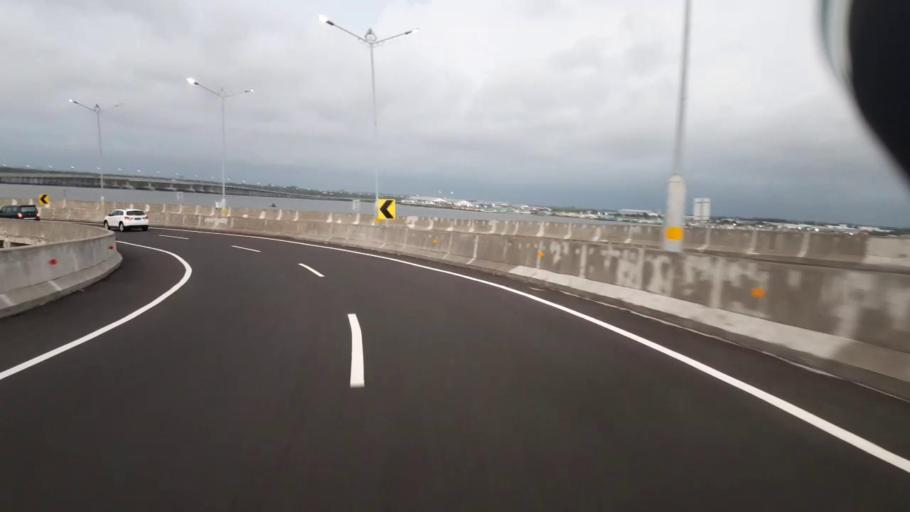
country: ID
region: Bali
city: Kelanabian
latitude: -8.7447
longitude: 115.1972
